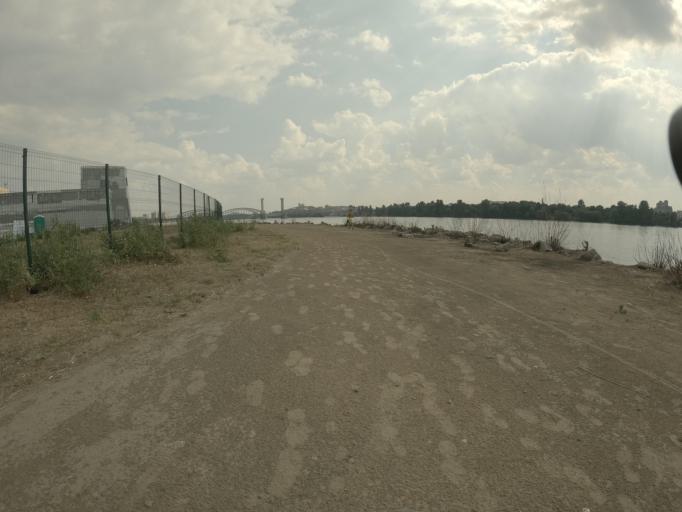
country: RU
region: St.-Petersburg
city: Centralniy
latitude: 59.9218
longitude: 30.4055
